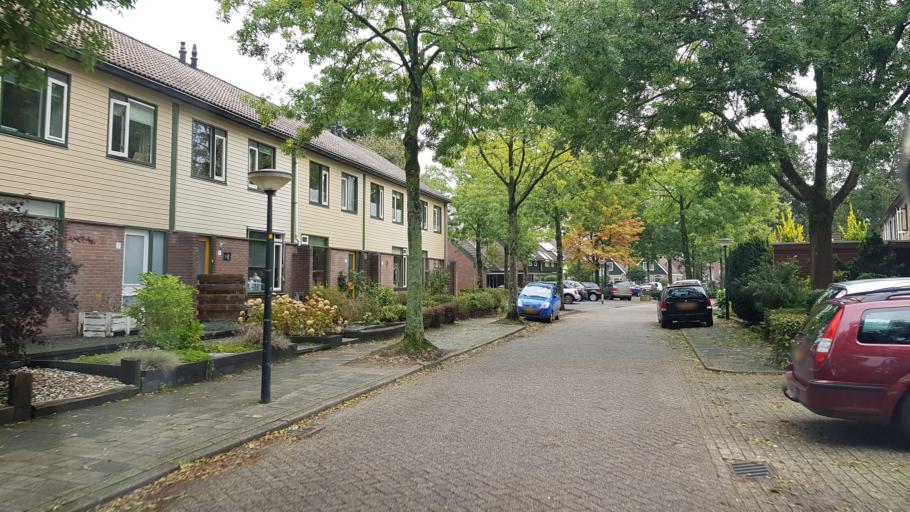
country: NL
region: Gelderland
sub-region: Gemeente Apeldoorn
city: Beekbergen
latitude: 52.1841
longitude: 5.9451
